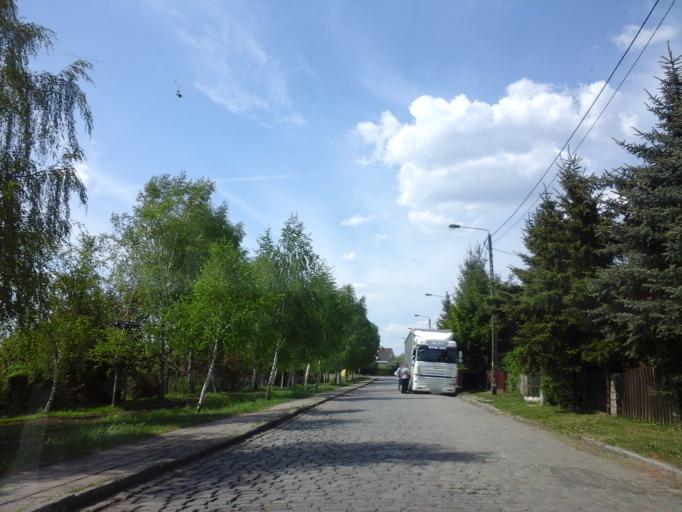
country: PL
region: West Pomeranian Voivodeship
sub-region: Powiat choszczenski
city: Choszczno
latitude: 53.1695
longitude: 15.4321
